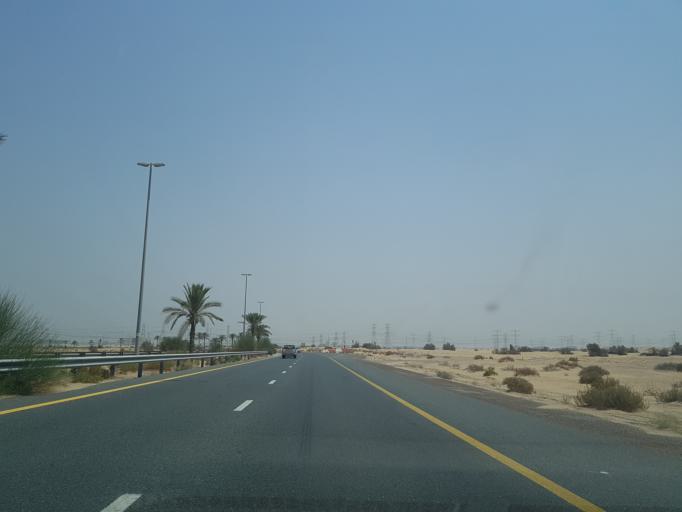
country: AE
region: Ash Shariqah
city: Sharjah
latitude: 25.1288
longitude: 55.4301
